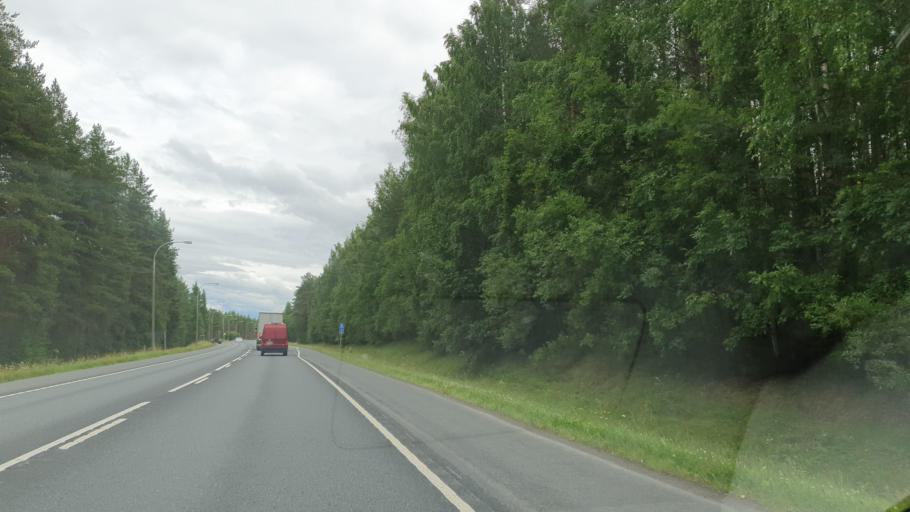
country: FI
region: Northern Savo
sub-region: Ylae-Savo
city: Iisalmi
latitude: 63.4914
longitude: 27.2773
